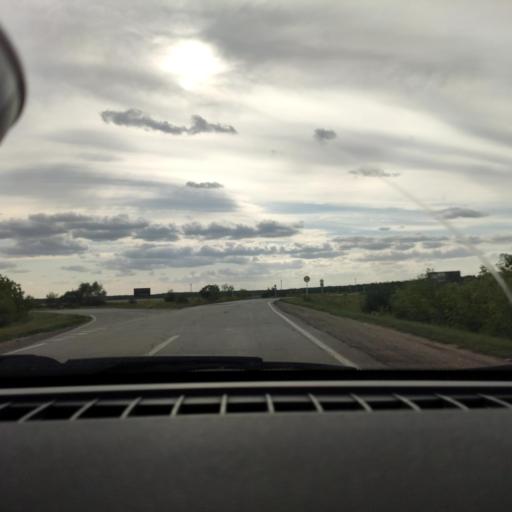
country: RU
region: Samara
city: Krasnyy Yar
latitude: 53.4321
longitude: 50.5472
